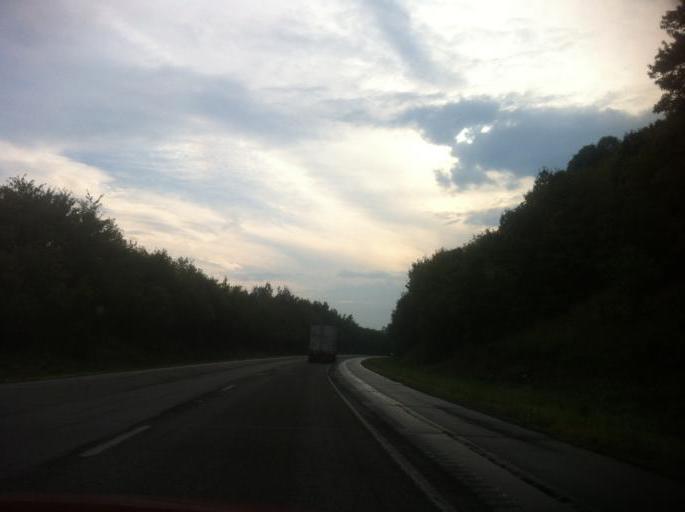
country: US
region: Pennsylvania
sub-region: Clarion County
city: Knox
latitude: 41.1875
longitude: -79.6003
